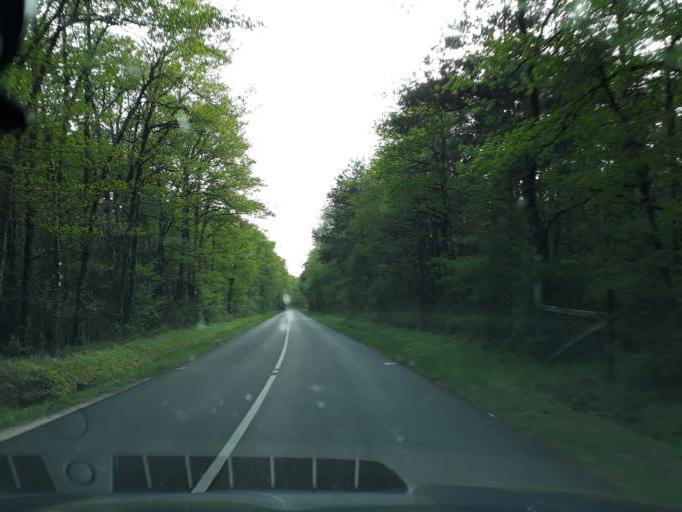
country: FR
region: Centre
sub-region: Departement du Loir-et-Cher
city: Muides-sur-Loire
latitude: 47.6510
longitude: 1.5831
